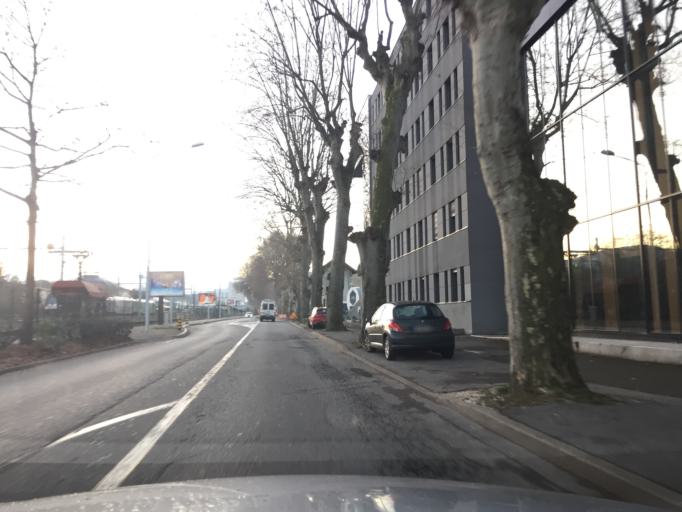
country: FR
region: Rhone-Alpes
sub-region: Departement de la Savoie
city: Cognin
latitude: 45.5801
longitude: 5.9124
